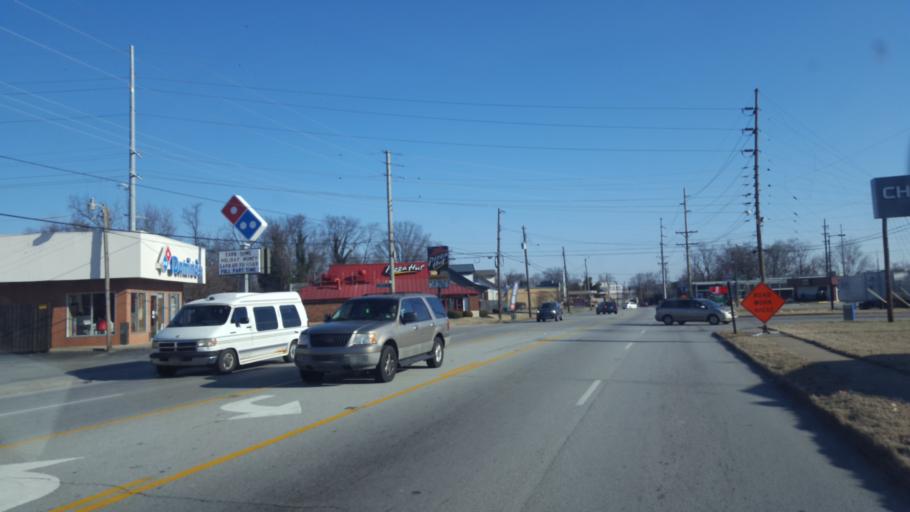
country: US
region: Kentucky
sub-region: Jefferson County
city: Shively
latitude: 38.1943
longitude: -85.8042
